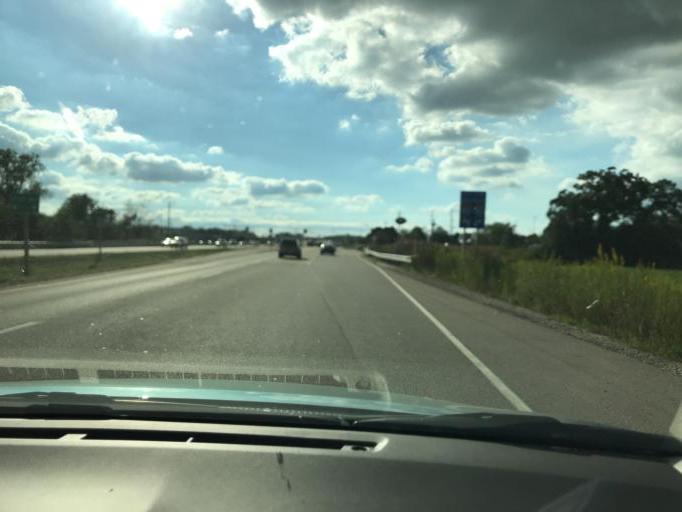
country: US
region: Wisconsin
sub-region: Kenosha County
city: Pleasant Prairie
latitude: 42.5676
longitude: -87.9448
